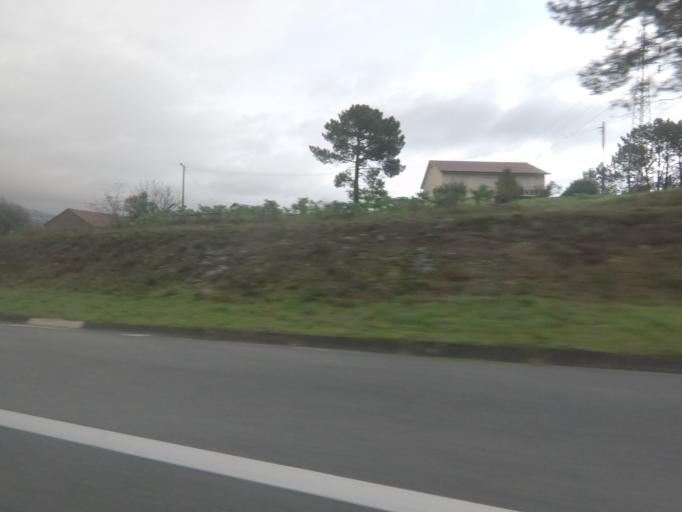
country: PT
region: Viana do Castelo
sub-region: Ponte de Lima
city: Ponte de Lima
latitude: 41.7614
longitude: -8.5606
